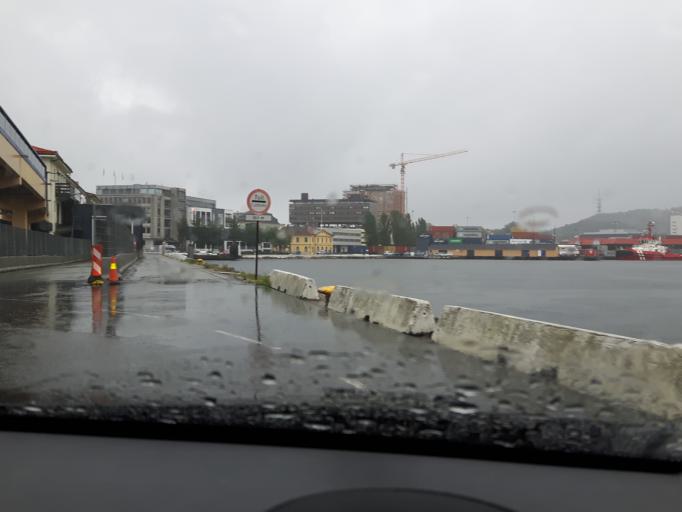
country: NO
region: Vest-Agder
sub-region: Kristiansand
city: Kristiansand
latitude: 58.1445
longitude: 7.9878
